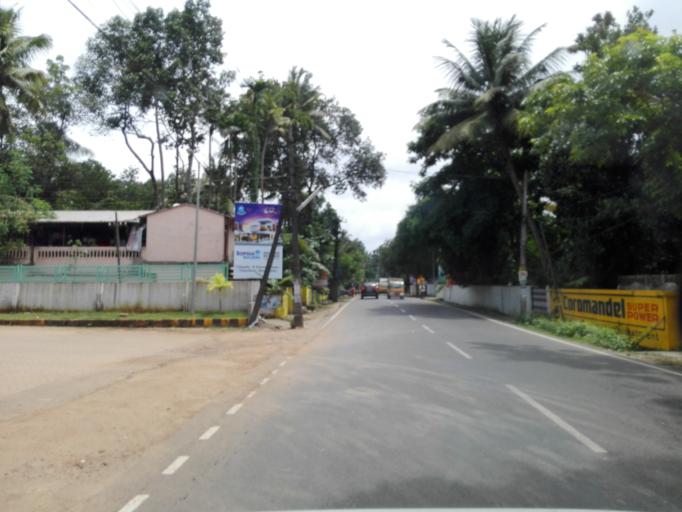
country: IN
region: Kerala
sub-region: Alappuzha
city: Arukutti
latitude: 9.8552
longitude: 76.3842
